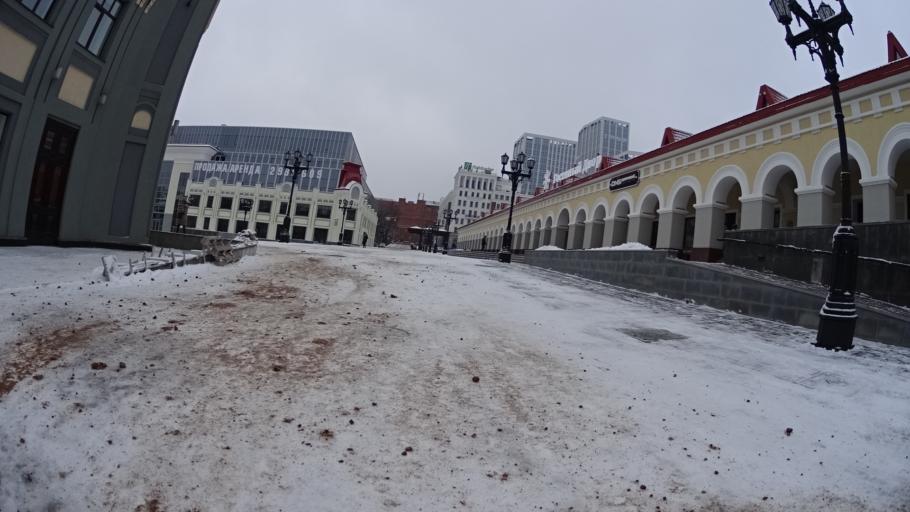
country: RU
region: Bashkortostan
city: Ufa
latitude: 54.7250
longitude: 55.9457
